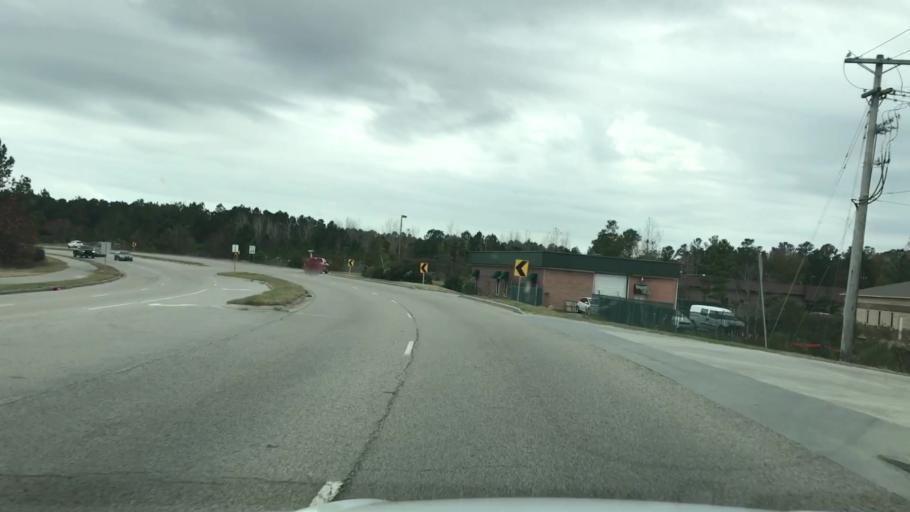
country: US
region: South Carolina
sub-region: Horry County
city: Forestbrook
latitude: 33.7105
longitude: -78.9401
